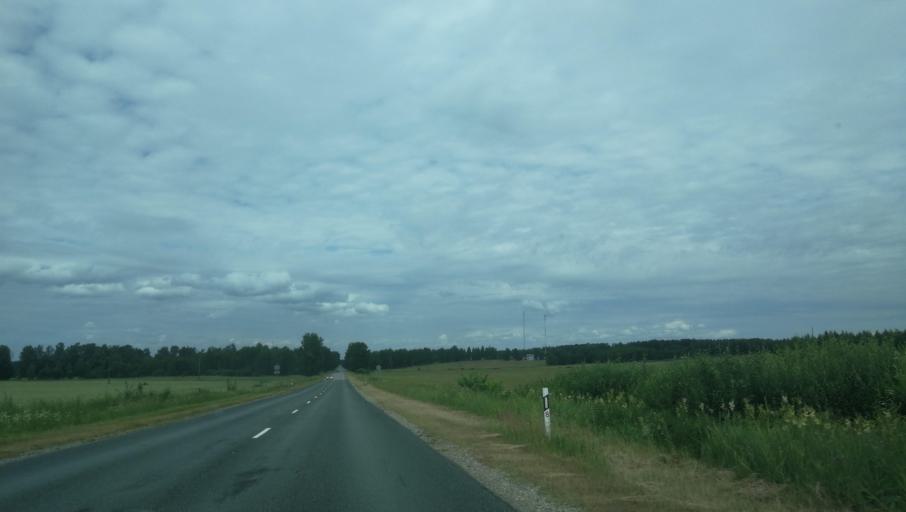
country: LV
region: Valmieras Rajons
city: Valmiera
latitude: 57.7068
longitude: 25.4262
